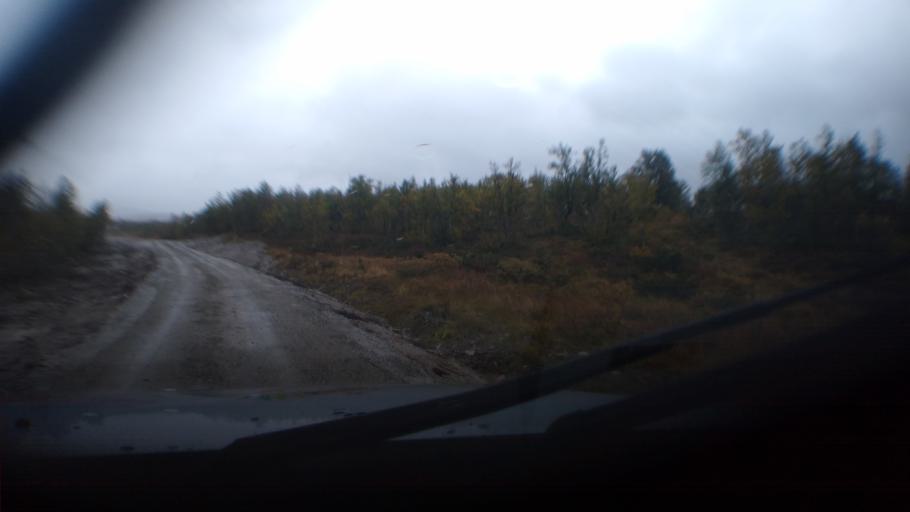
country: NO
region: Oppland
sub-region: Ringebu
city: Ringebu
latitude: 61.6564
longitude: 10.1035
